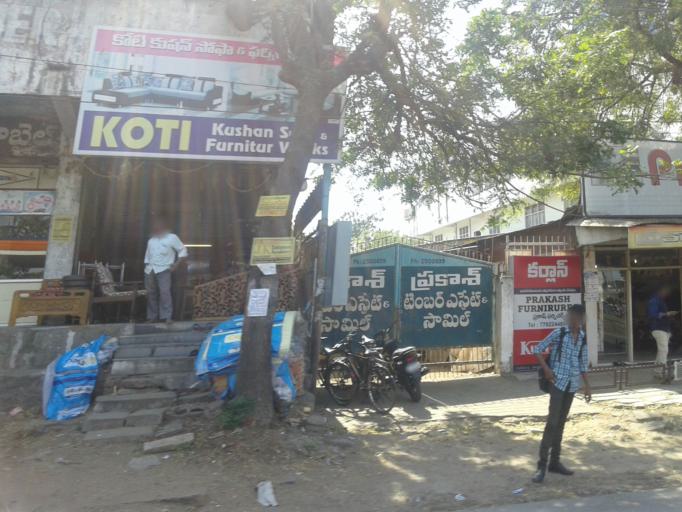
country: IN
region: Telangana
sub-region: Warangal
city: Warangal
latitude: 17.9999
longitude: 79.5837
